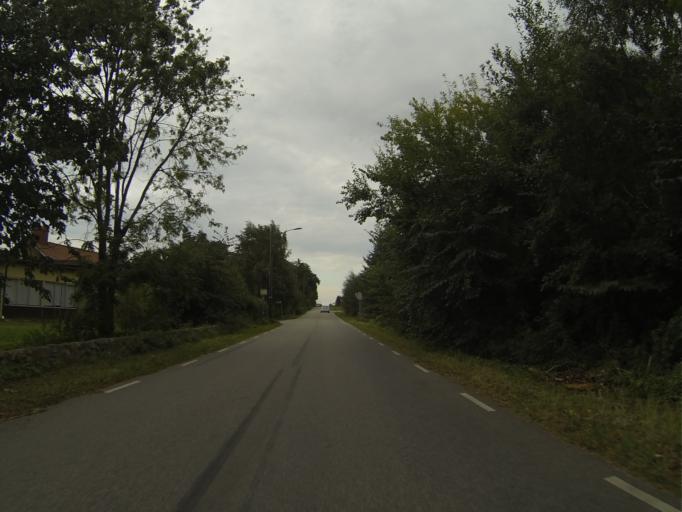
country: SE
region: Skane
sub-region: Staffanstorps Kommun
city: Hjaerup
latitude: 55.6248
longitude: 13.1255
